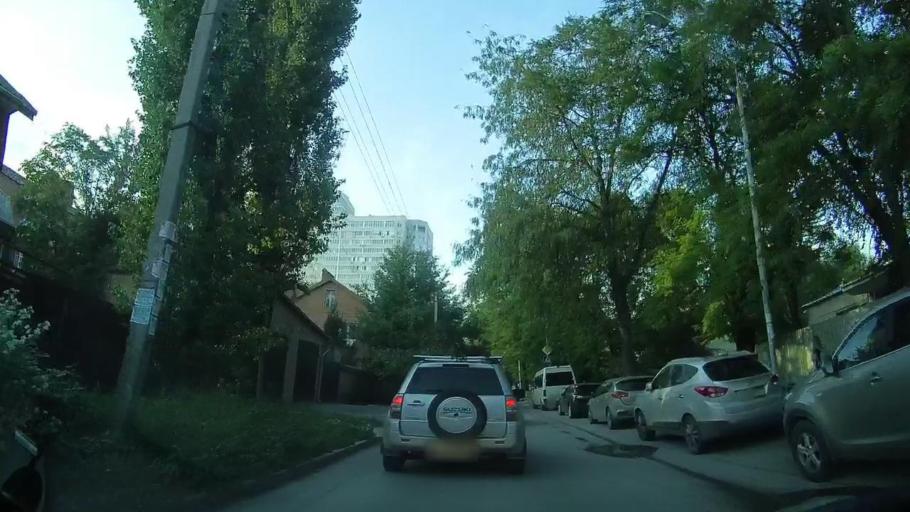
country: RU
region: Rostov
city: Rostov-na-Donu
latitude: 47.2331
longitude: 39.7080
